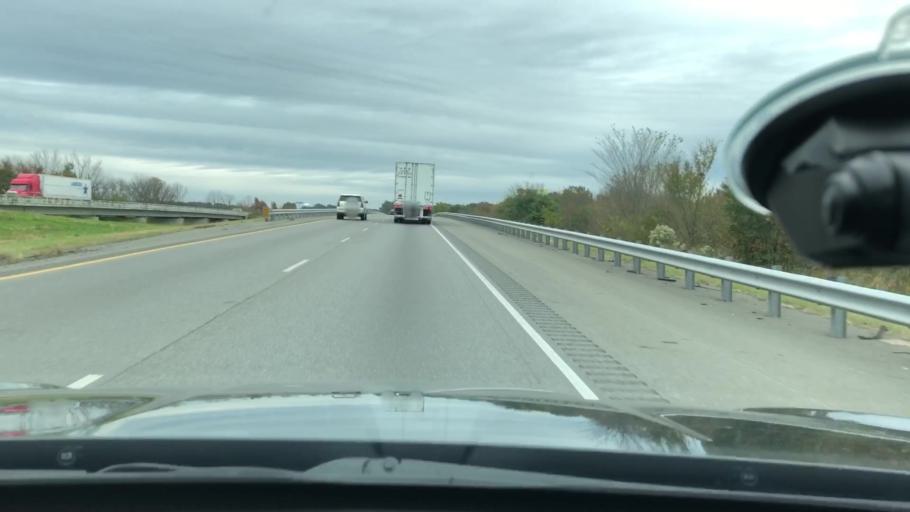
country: US
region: Arkansas
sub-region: Hempstead County
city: Hope
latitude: 33.6738
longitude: -93.6218
